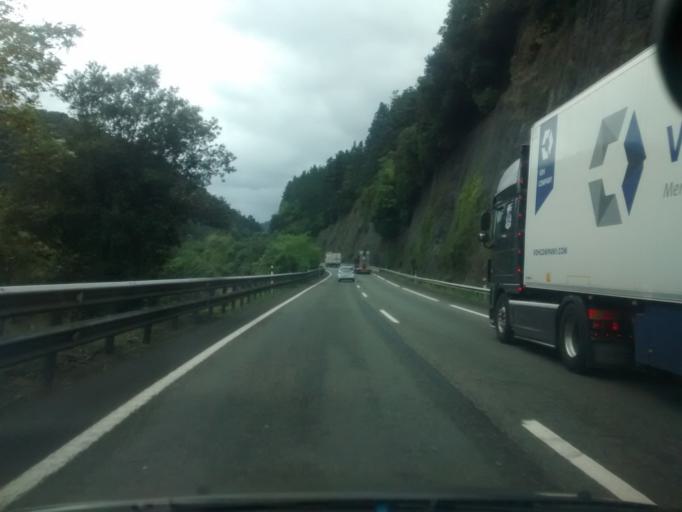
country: ES
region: Basque Country
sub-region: Provincia de Guipuzcoa
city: Mendaro
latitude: 43.2625
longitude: -2.3786
